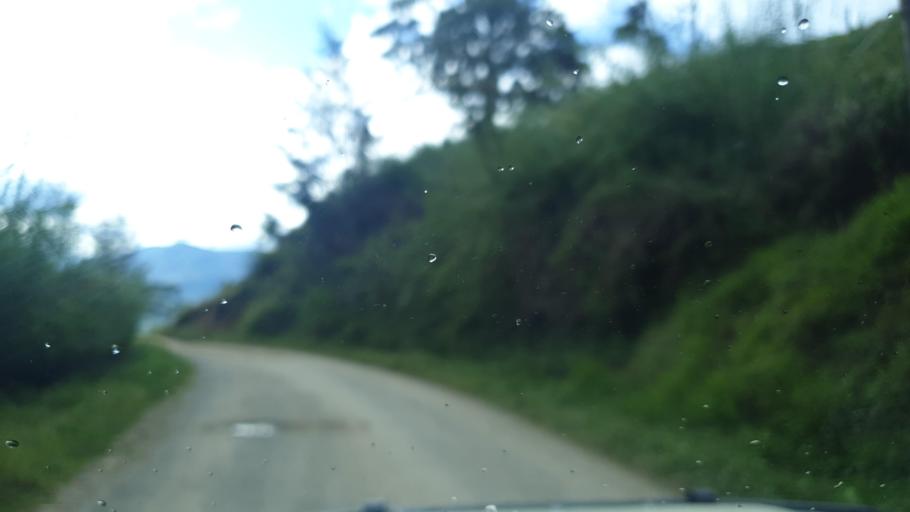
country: PG
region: Chimbu
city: Kundiawa
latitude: -6.1630
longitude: 145.1338
